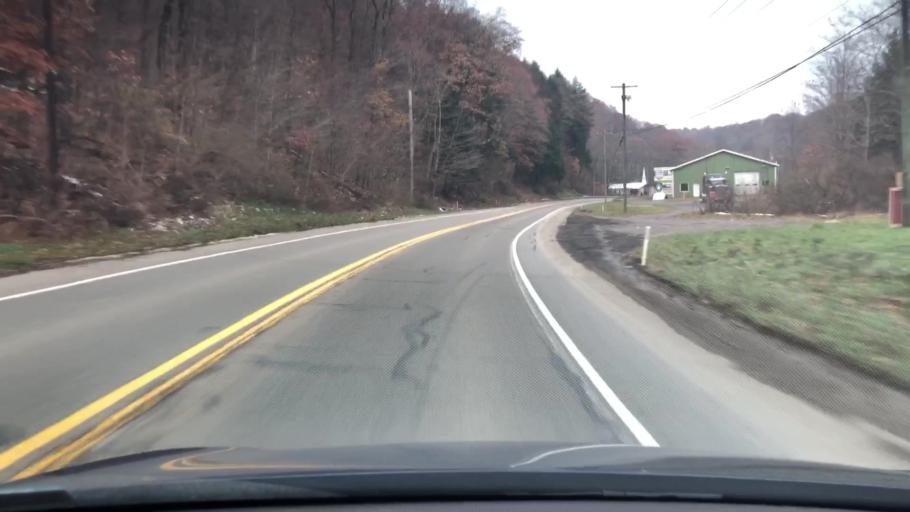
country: US
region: Pennsylvania
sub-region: Clarion County
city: Clarion
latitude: 40.9922
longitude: -79.3422
